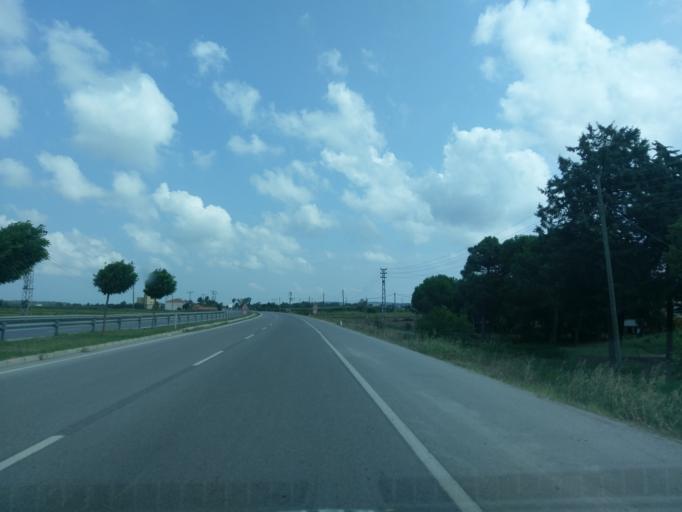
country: TR
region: Samsun
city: Bafra
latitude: 41.5993
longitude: 35.7812
